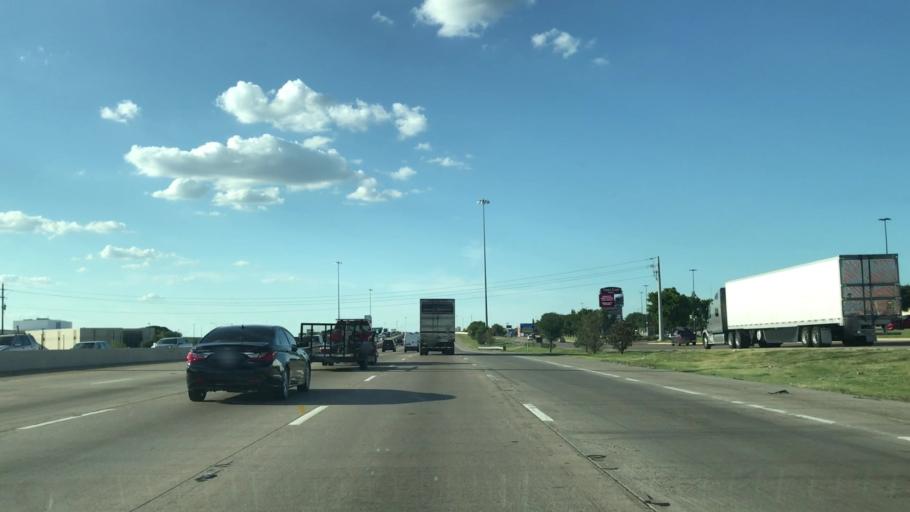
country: US
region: Texas
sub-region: Dallas County
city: Mesquite
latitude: 32.8050
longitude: -96.6268
